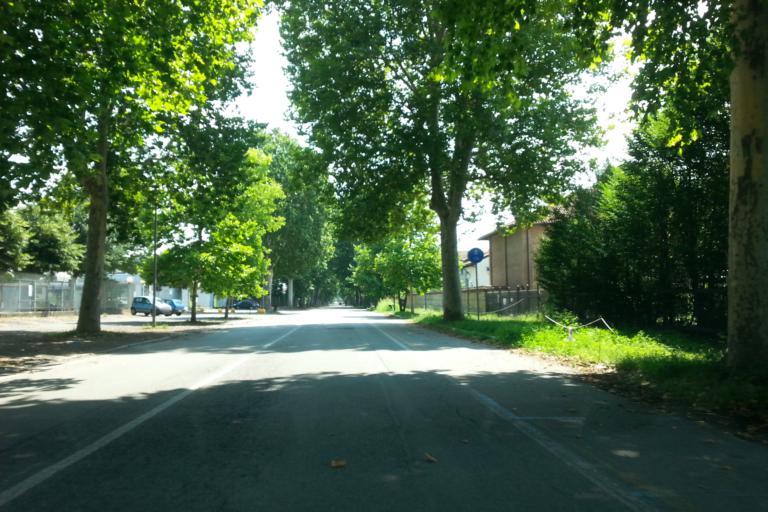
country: IT
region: Piedmont
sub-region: Provincia di Torino
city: Venaria Reale
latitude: 45.1400
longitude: 7.6166
